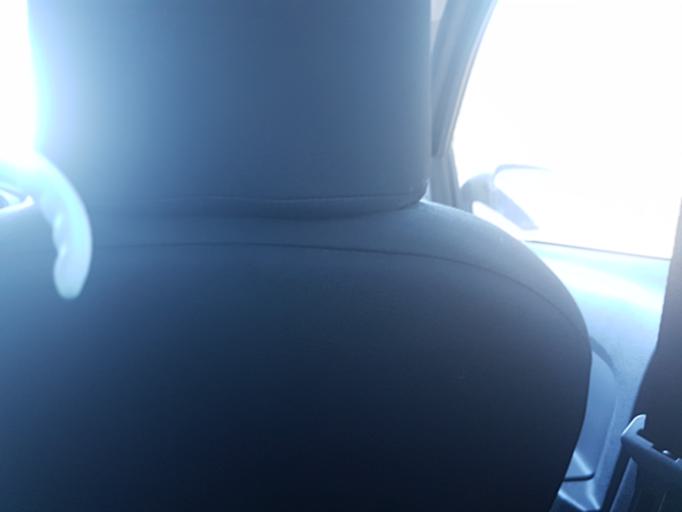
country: AR
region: Cordoba
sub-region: Departamento de Rio Segundo
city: Rio Segundo
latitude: -31.6322
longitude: -63.8739
